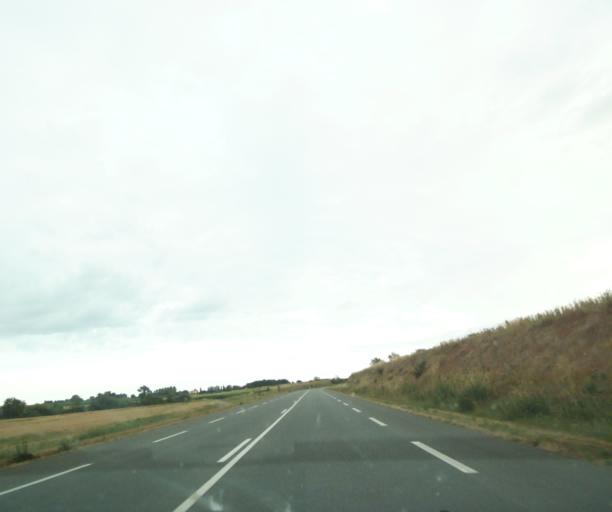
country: FR
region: Pays de la Loire
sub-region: Departement de la Vendee
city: Saint-Hilaire-de-Talmont
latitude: 46.4629
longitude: -1.6026
